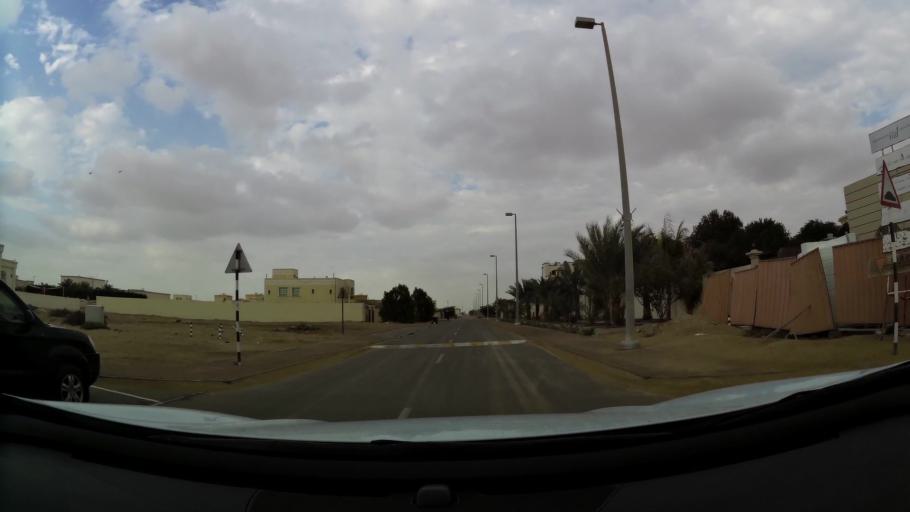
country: AE
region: Abu Dhabi
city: Abu Dhabi
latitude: 24.3515
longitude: 54.6139
